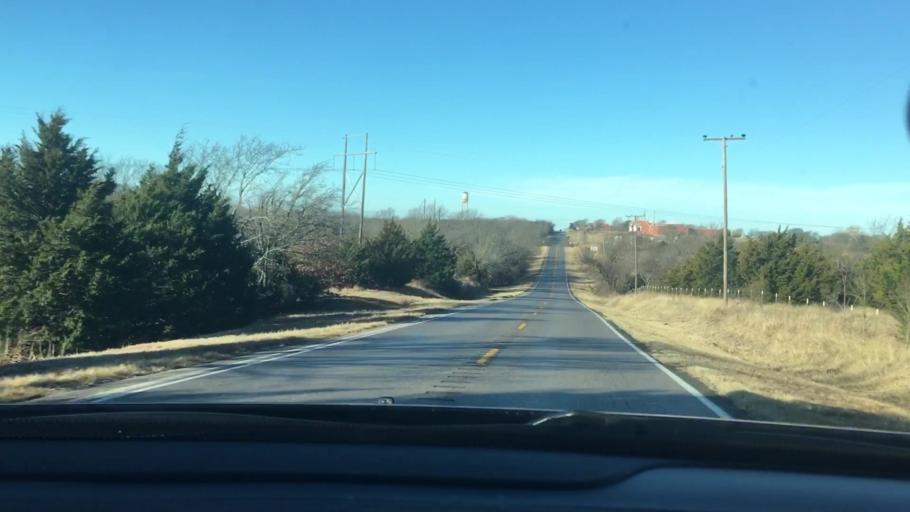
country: US
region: Oklahoma
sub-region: Murray County
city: Sulphur
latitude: 34.5109
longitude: -96.9417
